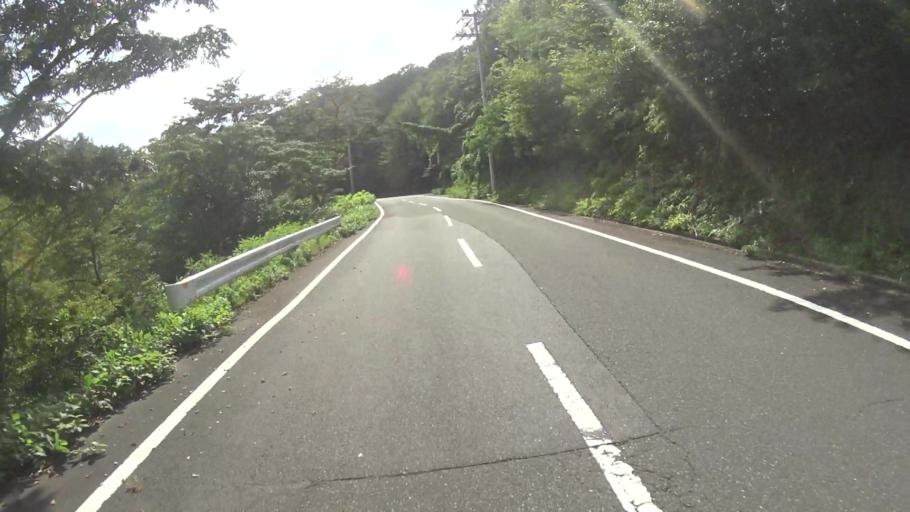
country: JP
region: Kyoto
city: Miyazu
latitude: 35.7255
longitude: 135.1881
